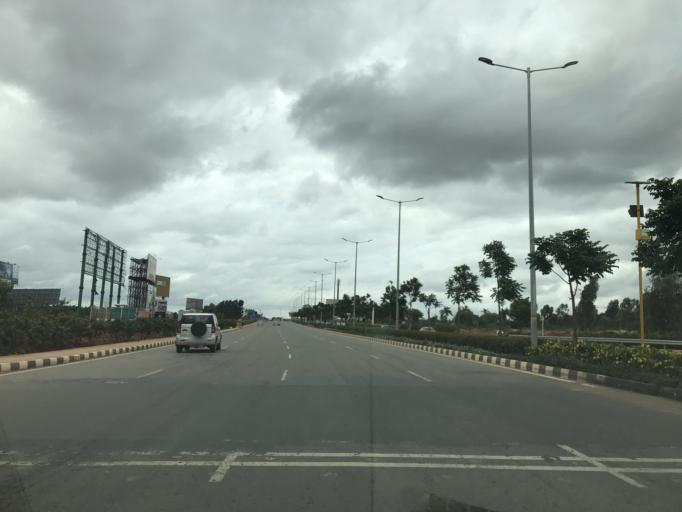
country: IN
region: Karnataka
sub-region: Bangalore Rural
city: Devanhalli
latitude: 13.1949
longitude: 77.6809
